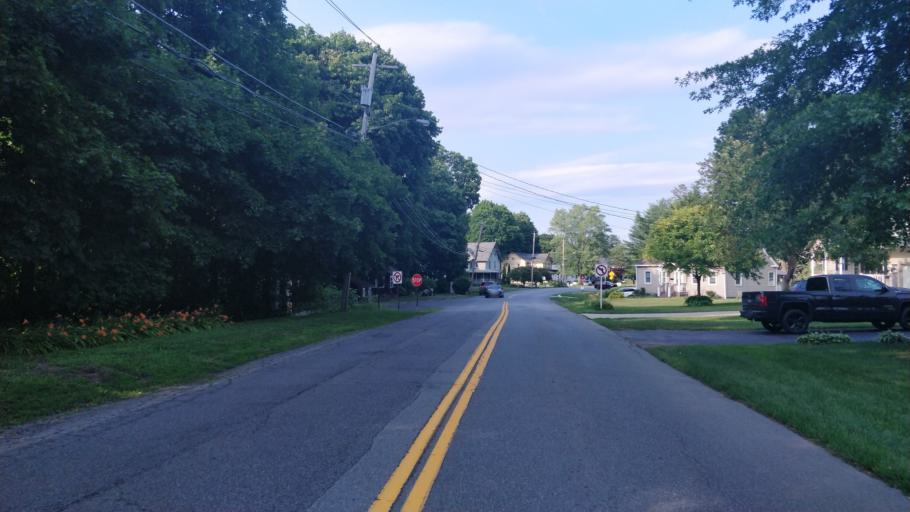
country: US
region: New York
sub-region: Saratoga County
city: Ballston Spa
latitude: 43.0086
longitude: -73.8433
